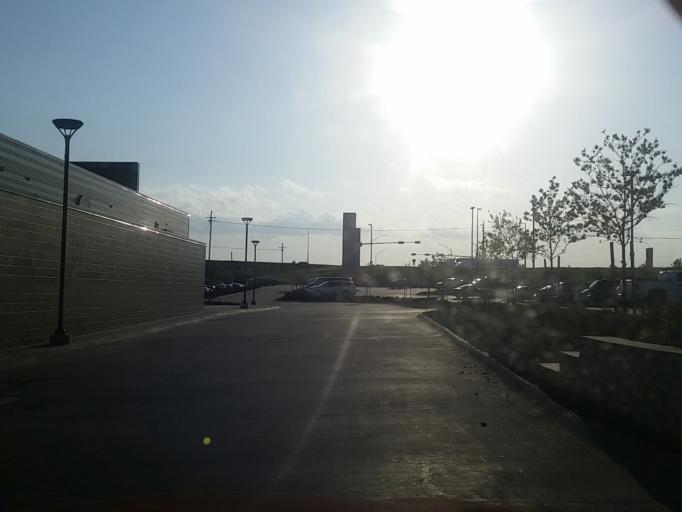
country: US
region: Nebraska
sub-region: Sarpy County
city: Gretna
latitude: 41.0995
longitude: -96.2510
